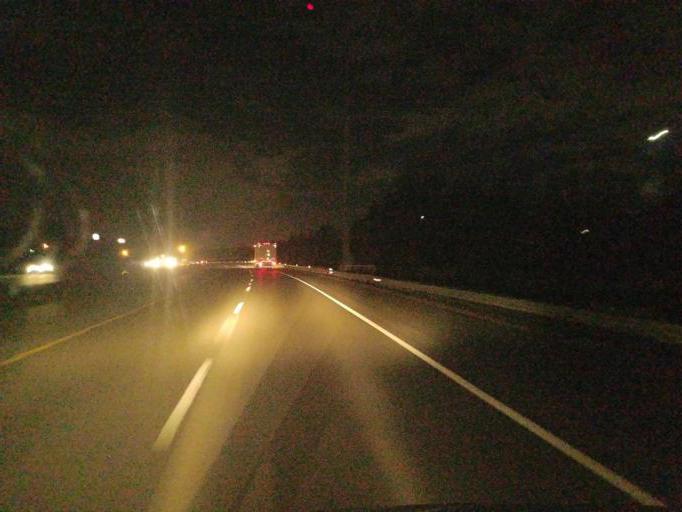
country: US
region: Ohio
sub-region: Montgomery County
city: Englewood
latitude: 39.8556
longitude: -84.2914
